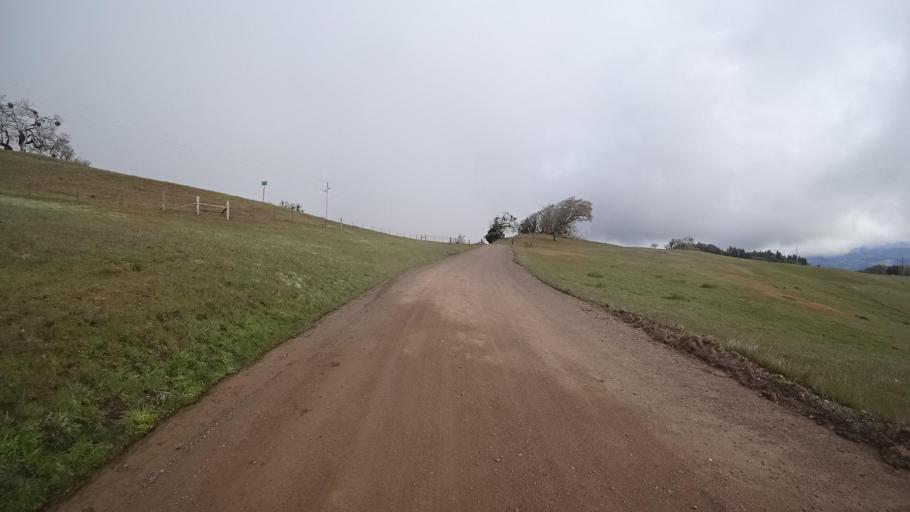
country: US
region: California
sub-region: Humboldt County
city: Redway
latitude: 40.1965
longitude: -123.7063
